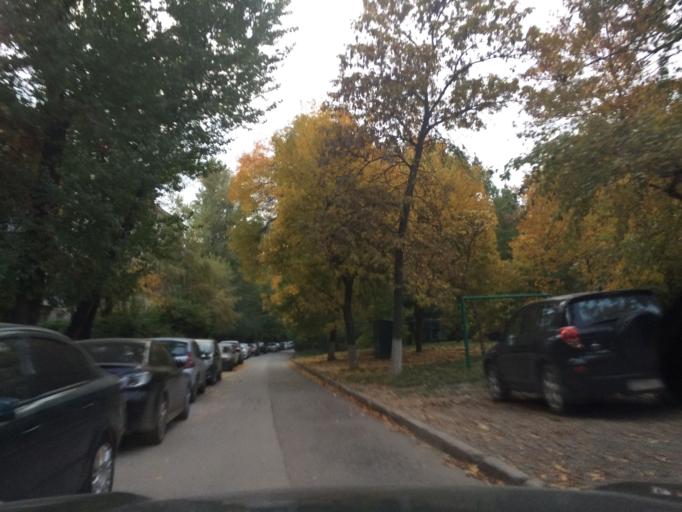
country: RU
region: Rostov
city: Rostov-na-Donu
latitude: 47.2017
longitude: 39.6206
